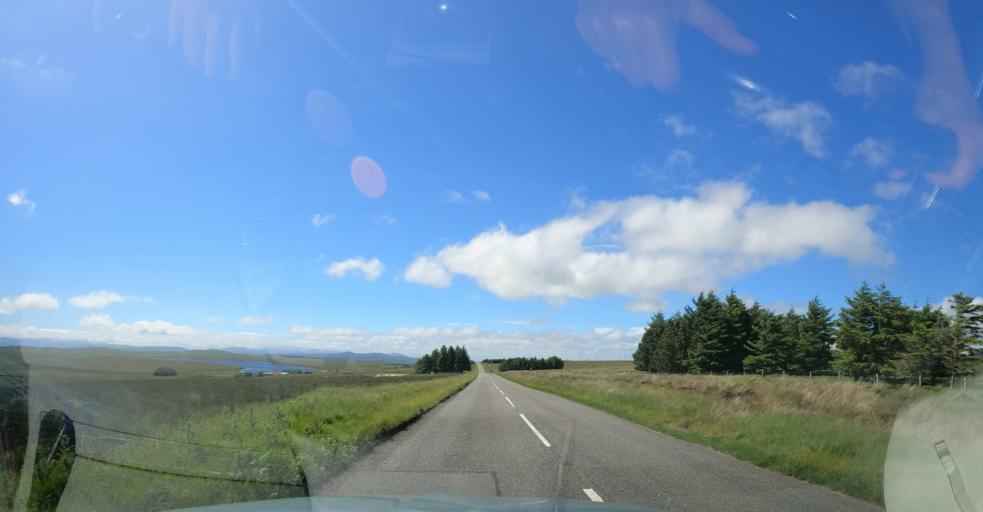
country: GB
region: Scotland
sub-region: Eilean Siar
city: Stornoway
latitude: 58.1732
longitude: -6.5966
